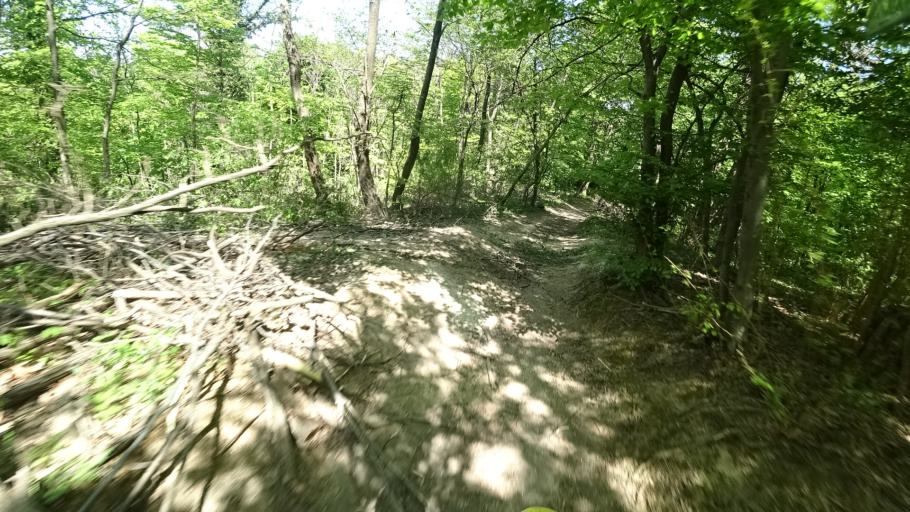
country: HR
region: Zagrebacka
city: Jablanovec
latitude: 45.8464
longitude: 15.8531
